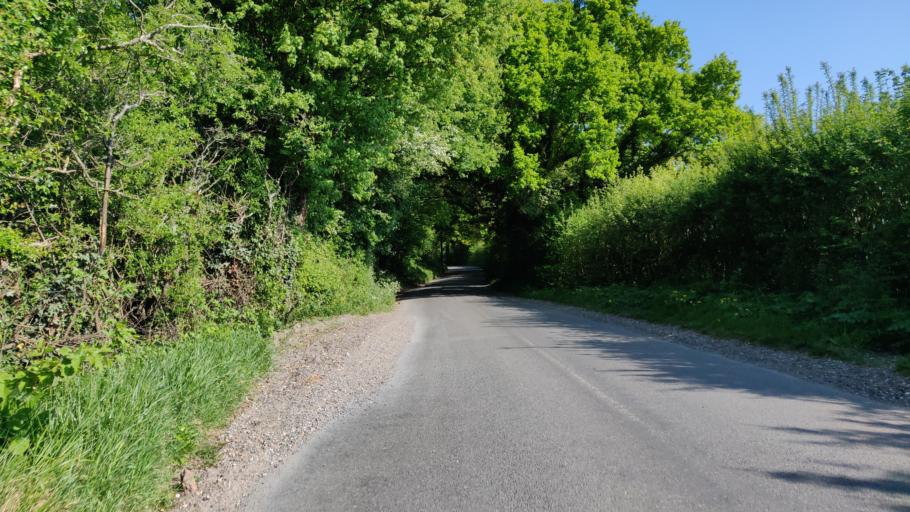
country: GB
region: England
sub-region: West Sussex
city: Billingshurst
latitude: 51.0270
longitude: -0.4160
